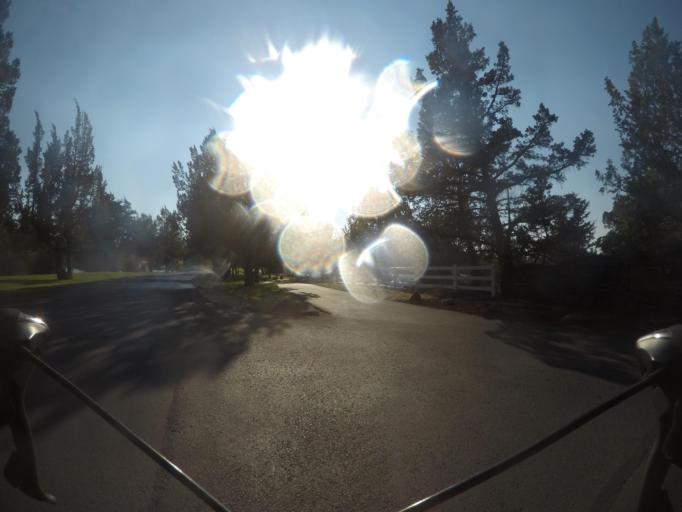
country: US
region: Oregon
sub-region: Deschutes County
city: Redmond
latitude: 44.2636
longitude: -121.2580
